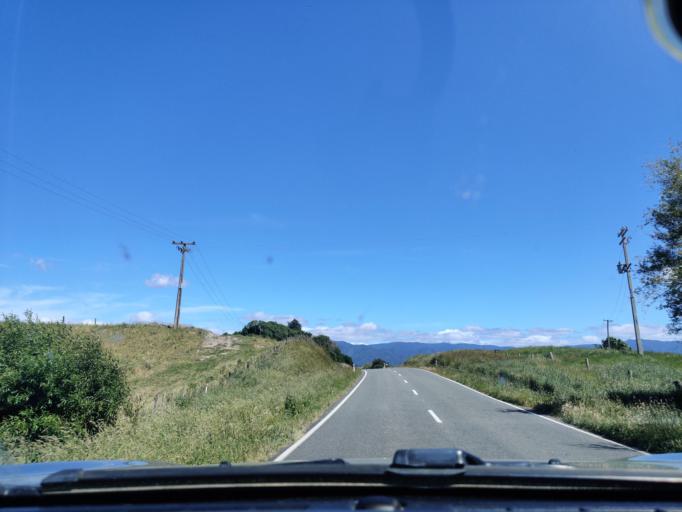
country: NZ
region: Wellington
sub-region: Upper Hutt City
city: Upper Hutt
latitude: -41.3275
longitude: 175.2294
